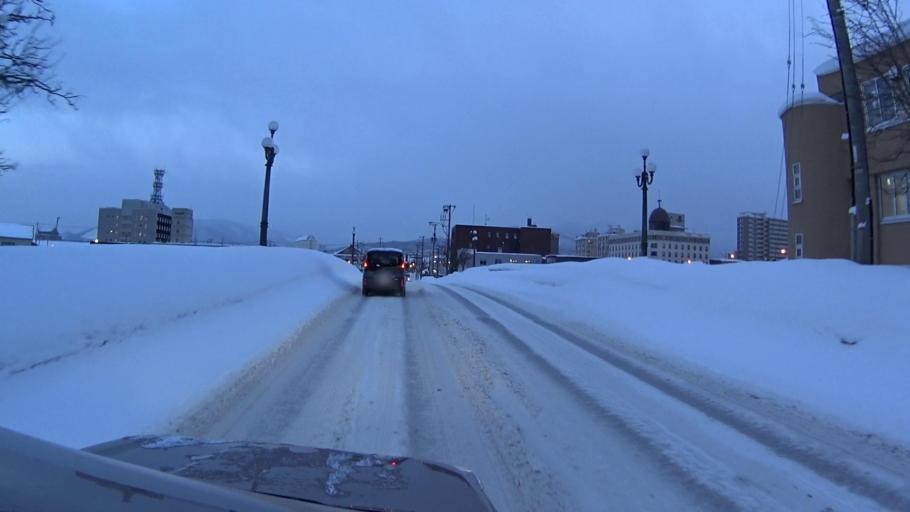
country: JP
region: Hokkaido
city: Otaru
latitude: 43.2018
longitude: 141.0013
